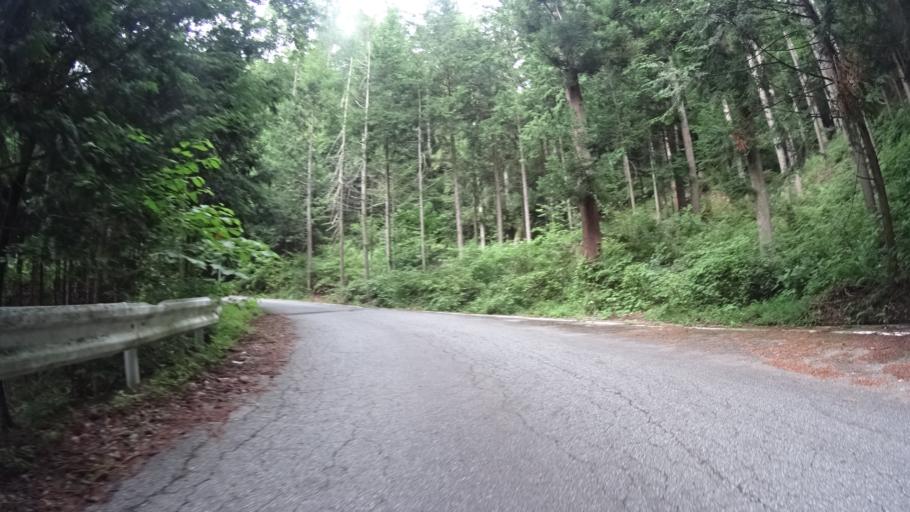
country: JP
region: Yamanashi
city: Kofu-shi
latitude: 35.8029
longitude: 138.5913
